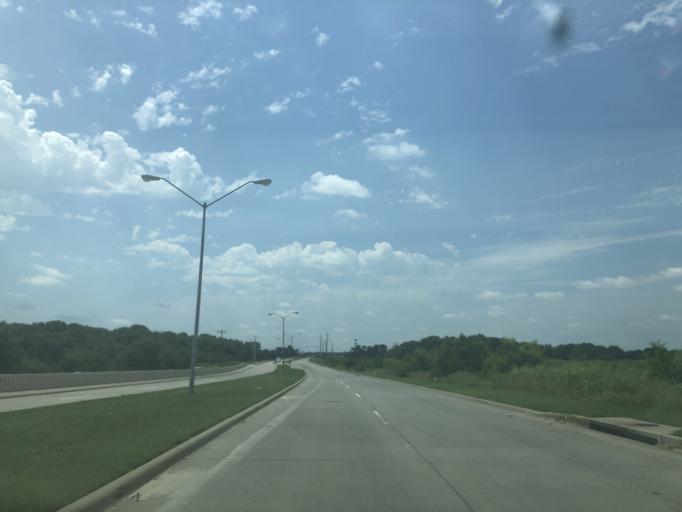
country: US
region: Texas
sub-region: Dallas County
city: Irving
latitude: 32.7782
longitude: -96.9603
